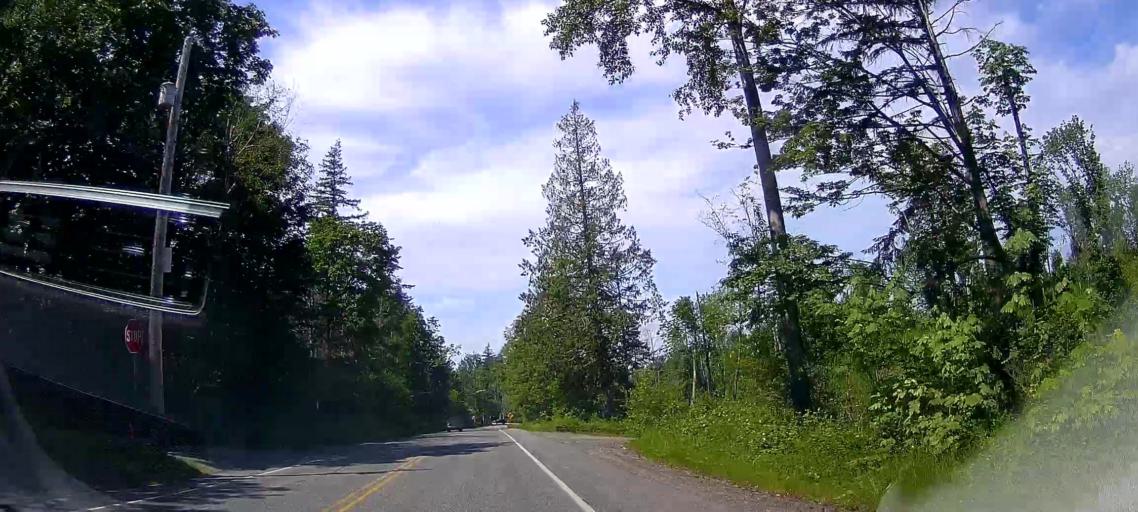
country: US
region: Washington
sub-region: Skagit County
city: Mount Vernon
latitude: 48.4013
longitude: -122.3040
